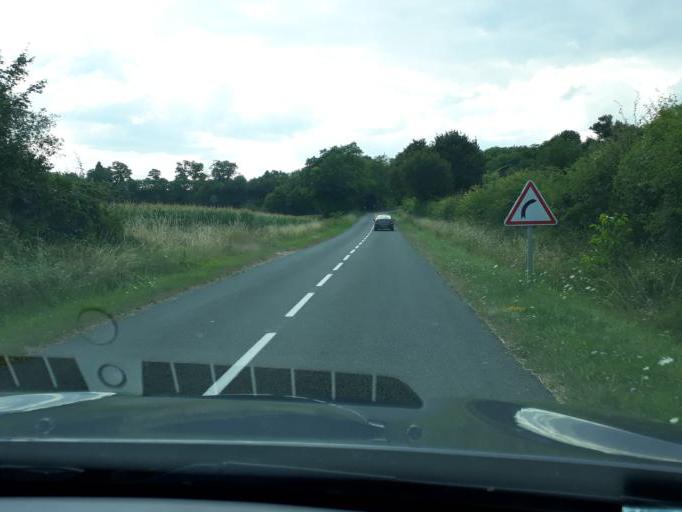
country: FR
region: Centre
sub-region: Departement du Cher
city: Nerondes
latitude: 47.0638
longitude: 2.8066
